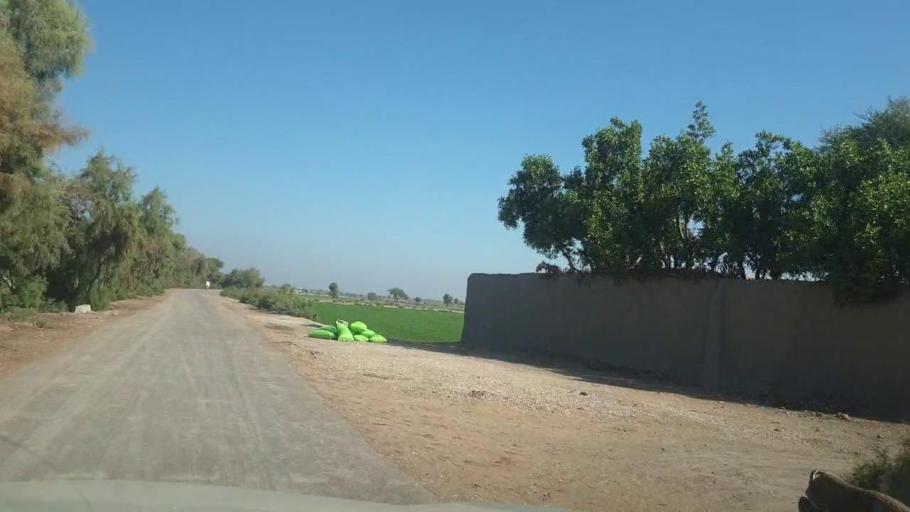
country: PK
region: Sindh
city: Bhan
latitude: 26.5330
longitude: 67.6439
